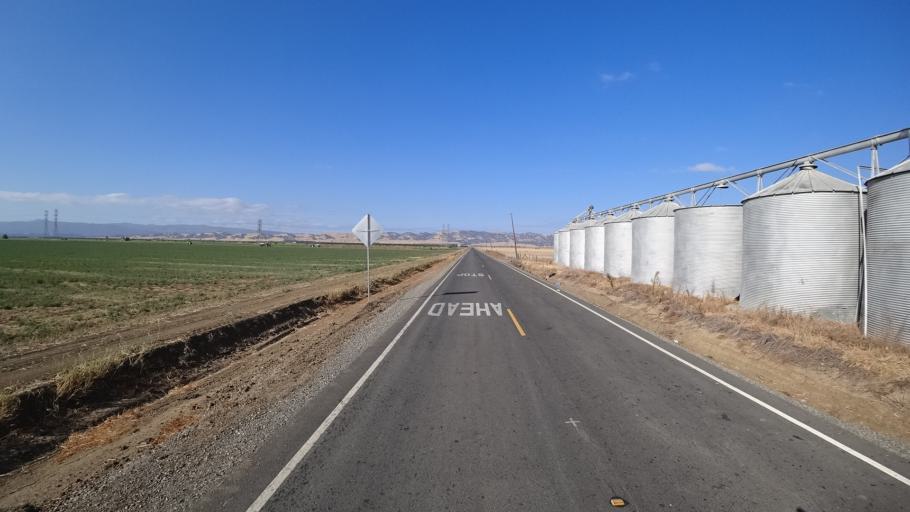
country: US
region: California
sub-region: Yolo County
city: Esparto
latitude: 38.7808
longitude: -122.0090
